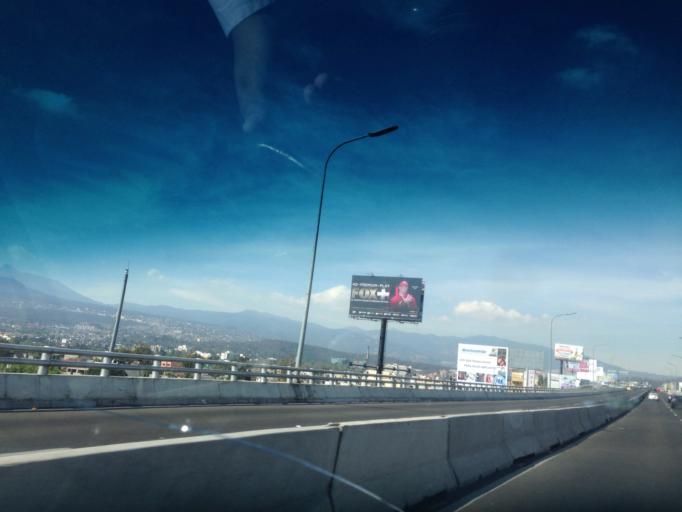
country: MX
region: Mexico City
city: Tlalpan
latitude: 19.3020
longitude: -99.1667
